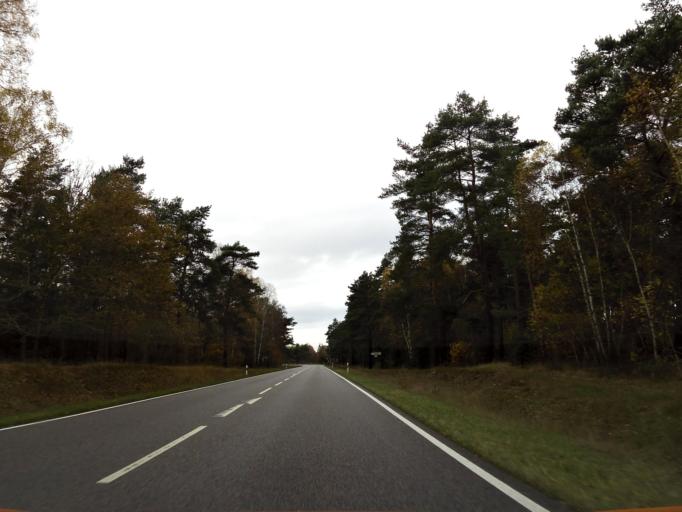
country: DE
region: Saxony-Anhalt
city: Colbitz
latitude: 52.3561
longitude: 11.5403
